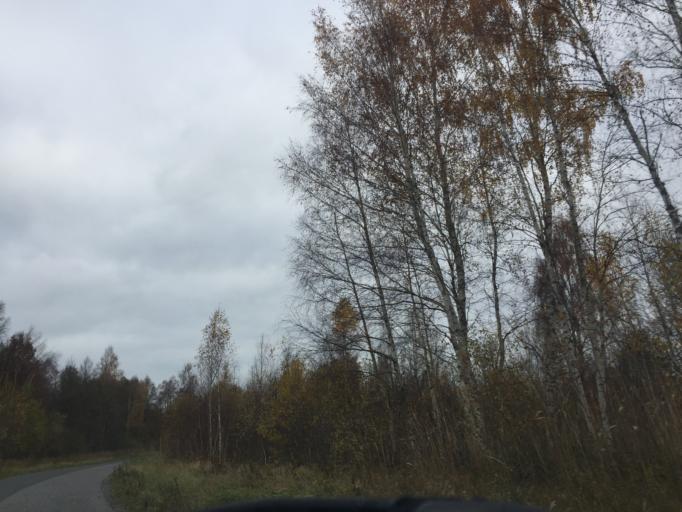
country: LV
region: Liepaja
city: Vec-Liepaja
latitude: 56.5546
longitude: 21.0652
